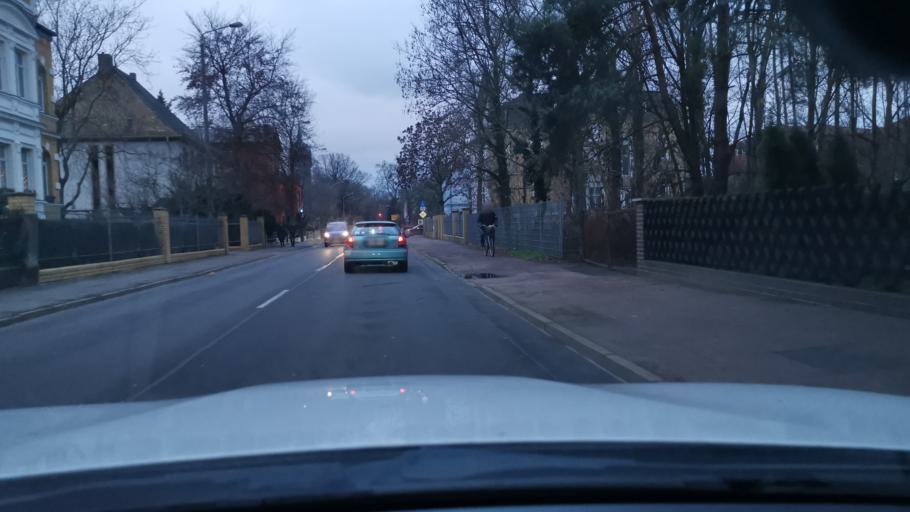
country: DE
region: Saxony-Anhalt
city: Wittenburg
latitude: 51.8711
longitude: 12.6356
